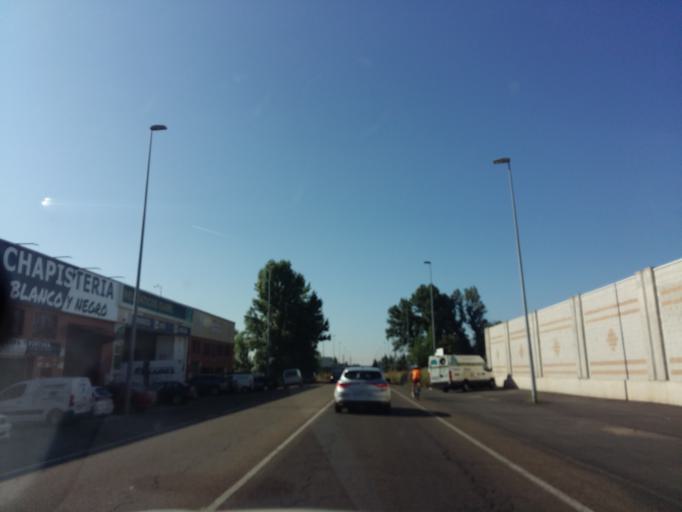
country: ES
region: Castille and Leon
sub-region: Provincia de Leon
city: Leon
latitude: 42.5751
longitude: -5.5832
